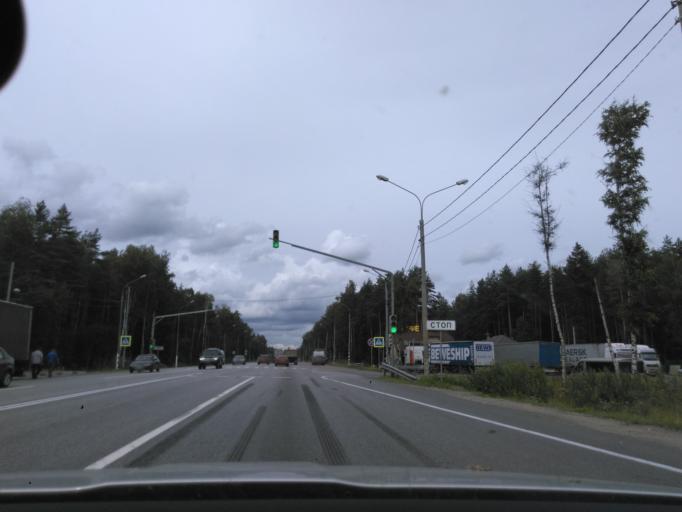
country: RU
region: Moskovskaya
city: Reshetnikovo
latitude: 56.4234
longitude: 36.6300
